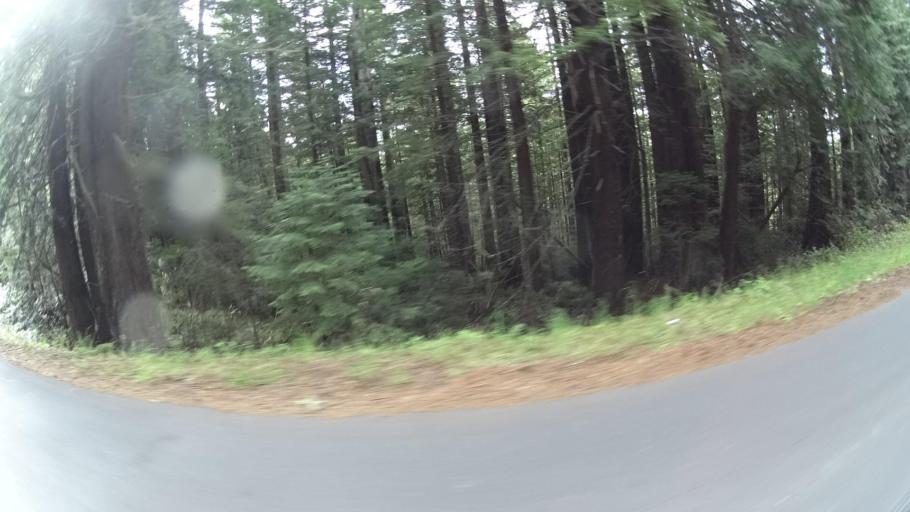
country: US
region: California
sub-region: Humboldt County
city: Bayside
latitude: 40.7580
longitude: -124.0272
